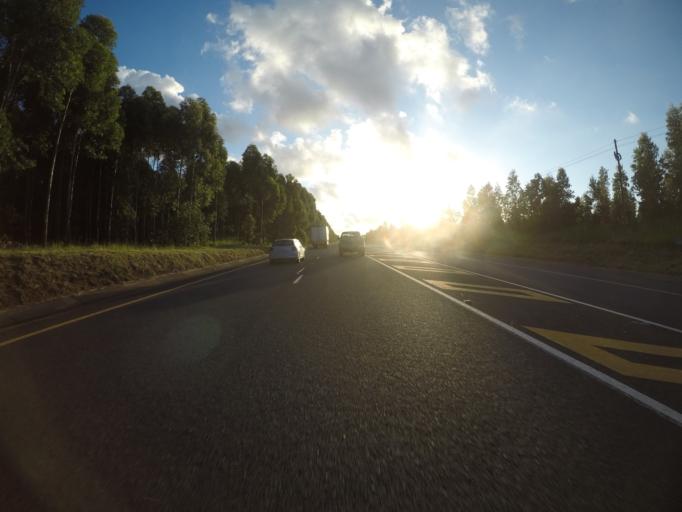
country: ZA
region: KwaZulu-Natal
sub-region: uThungulu District Municipality
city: Richards Bay
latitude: -28.6940
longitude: 31.9863
